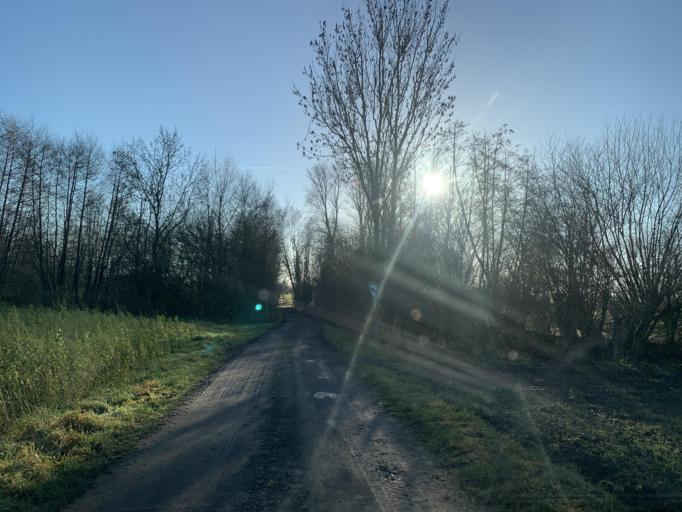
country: DE
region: North Rhine-Westphalia
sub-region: Regierungsbezirk Munster
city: Dulmen
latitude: 51.8768
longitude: 7.2737
